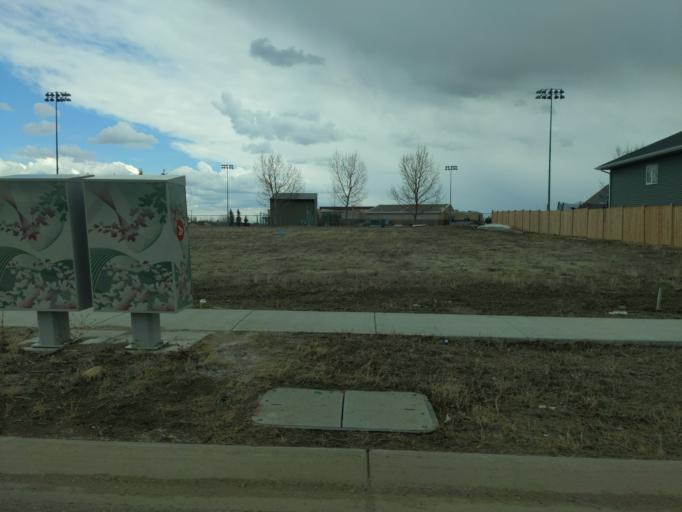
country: CA
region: Saskatchewan
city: Lloydminster
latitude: 53.2709
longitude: -110.0466
